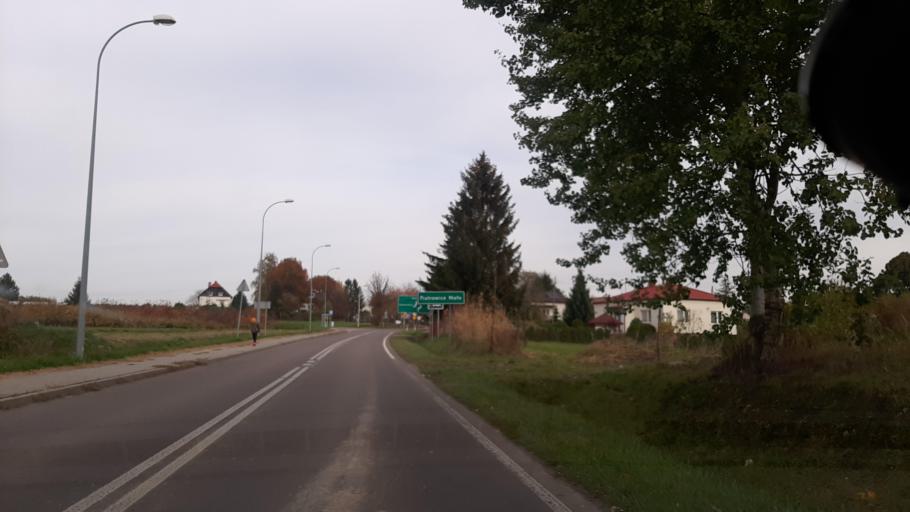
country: PL
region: Lublin Voivodeship
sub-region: Powiat pulawski
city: Naleczow
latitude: 51.3179
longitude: 22.2226
